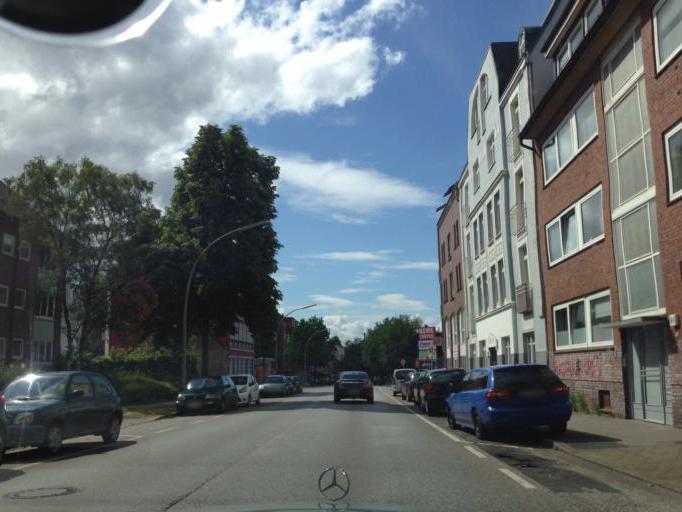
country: DE
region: Hamburg
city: Marienthal
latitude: 53.5817
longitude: 10.0803
